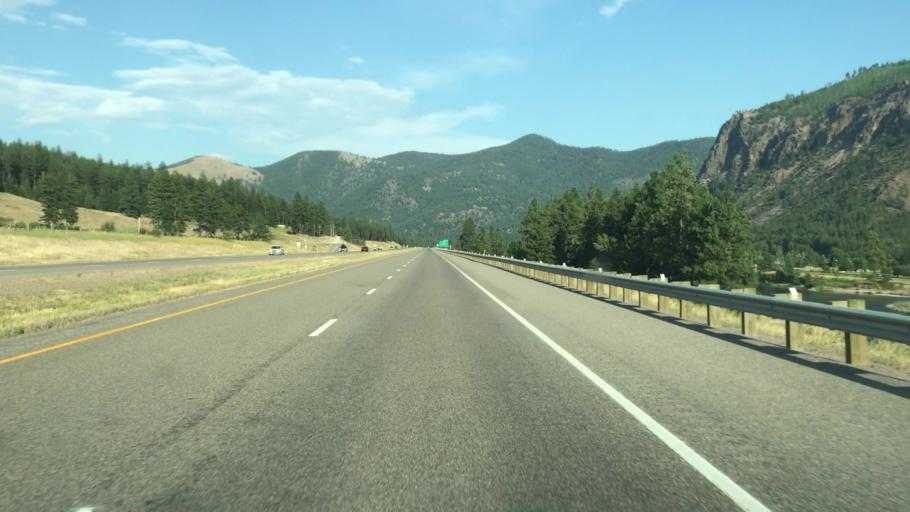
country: US
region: Montana
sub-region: Missoula County
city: Frenchtown
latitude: 46.9961
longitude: -114.4584
